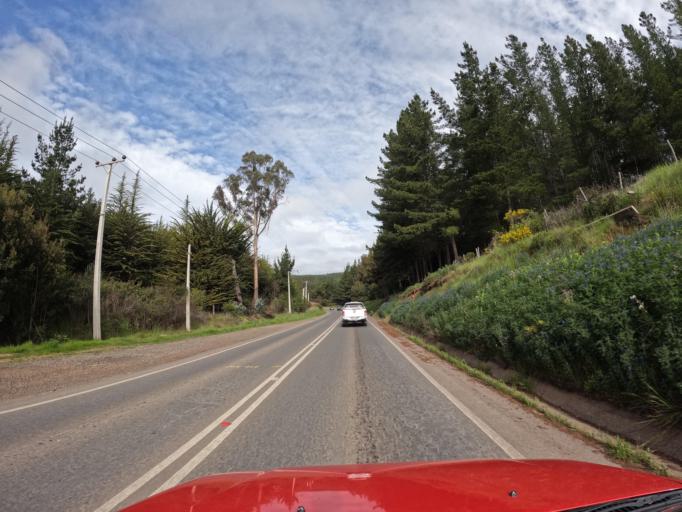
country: CL
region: O'Higgins
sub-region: Provincia de Colchagua
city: Santa Cruz
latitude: -34.3548
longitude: -71.9201
